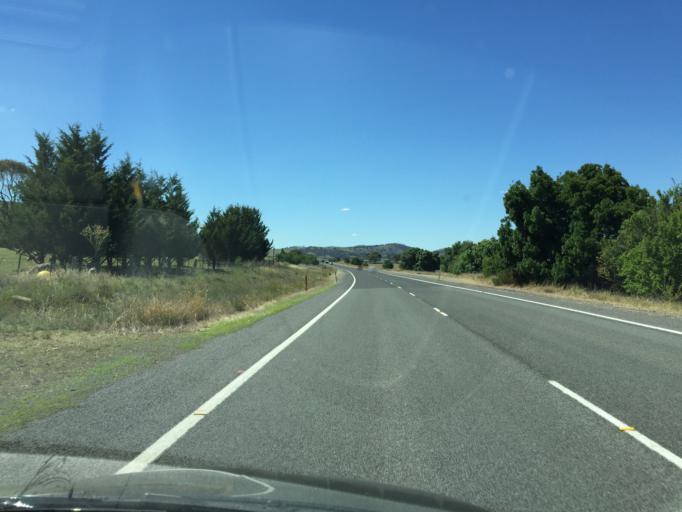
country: AU
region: Australian Capital Territory
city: Macarthur
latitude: -35.7321
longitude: 149.1607
